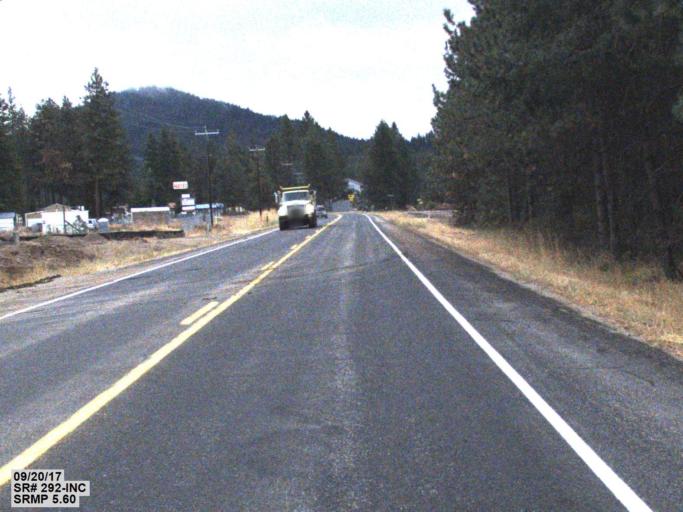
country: US
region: Washington
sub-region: Spokane County
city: Deer Park
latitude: 48.0598
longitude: -117.6270
